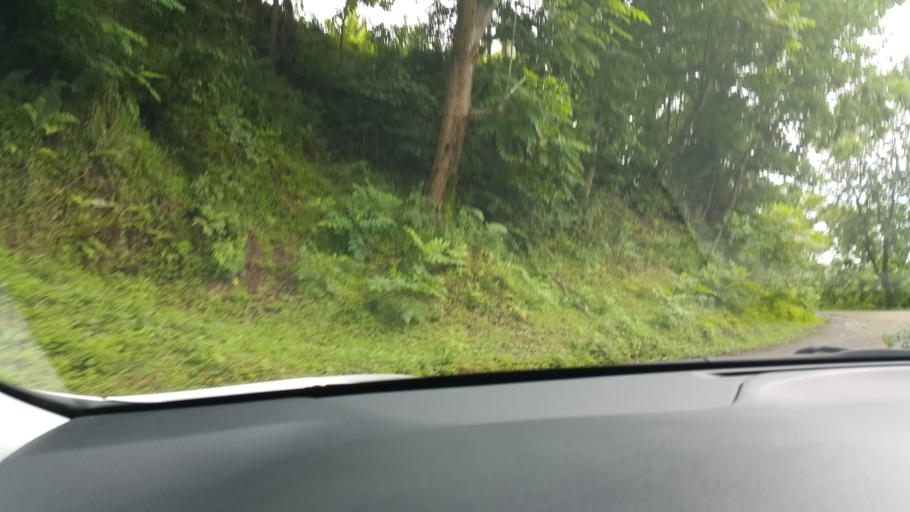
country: GE
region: Ajaria
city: Khelvachauri
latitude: 41.6148
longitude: 41.6565
